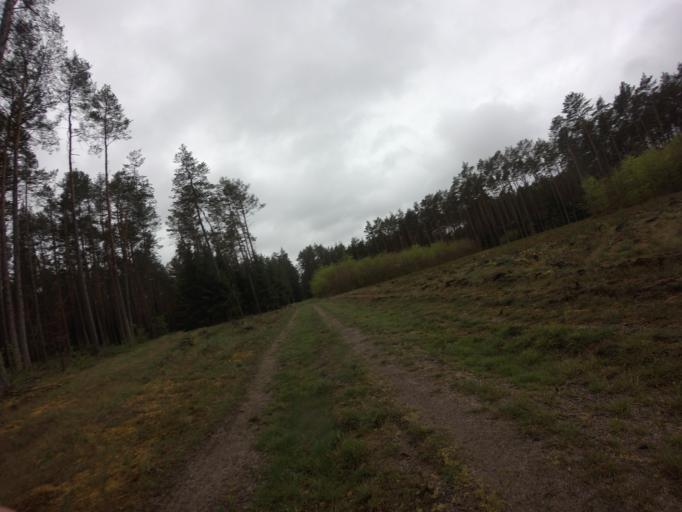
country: PL
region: West Pomeranian Voivodeship
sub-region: Powiat drawski
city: Kalisz Pomorski
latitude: 53.2166
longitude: 16.0140
